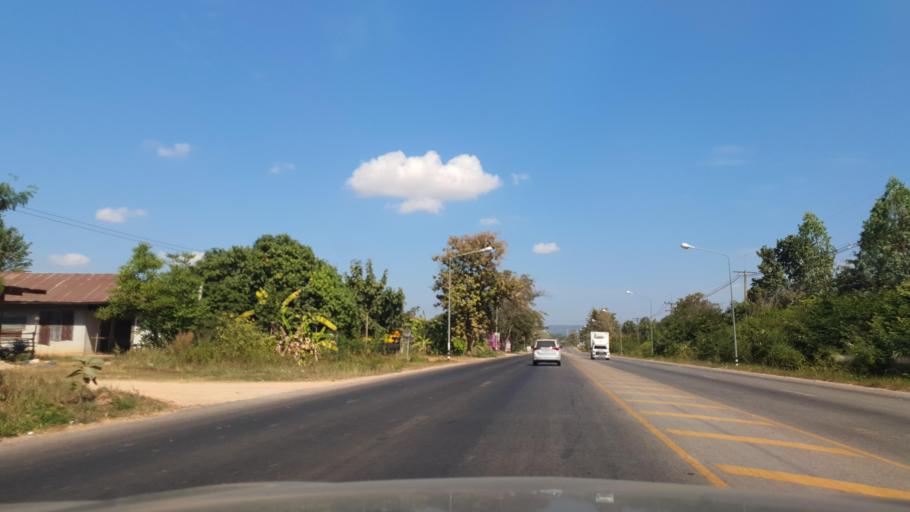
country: TH
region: Kalasin
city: Somdet
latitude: 16.7316
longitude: 103.7644
